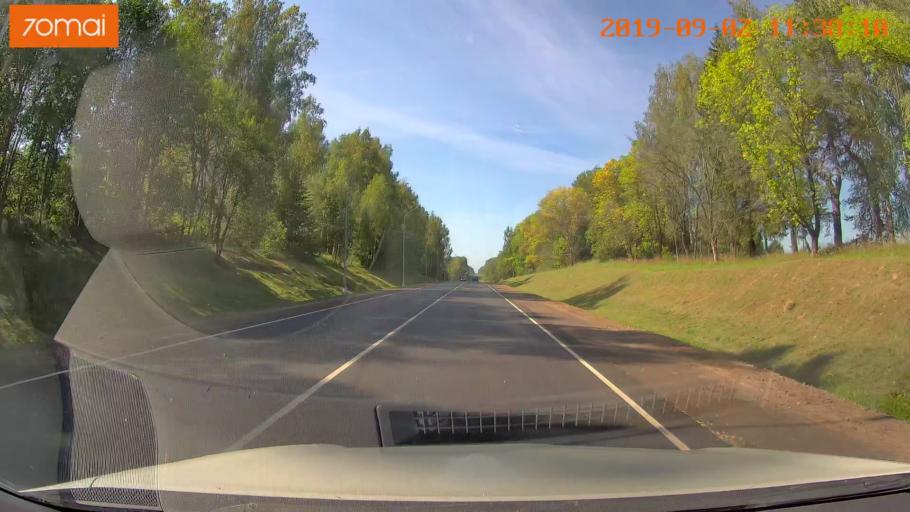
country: RU
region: Smolensk
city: Oster
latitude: 53.9147
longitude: 32.7454
